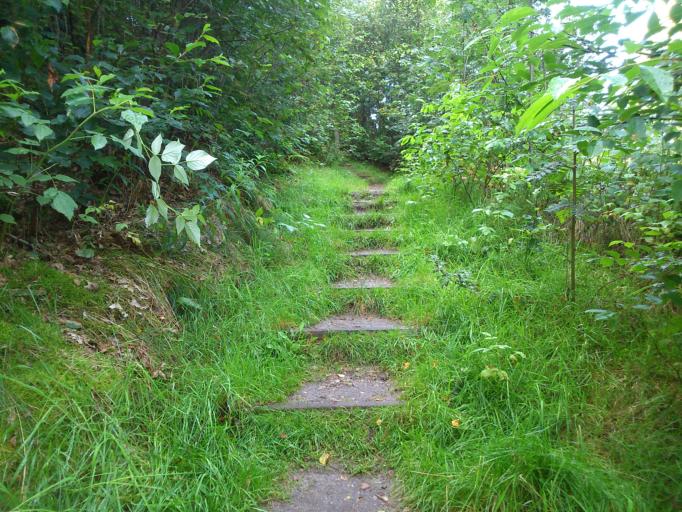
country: DK
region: Central Jutland
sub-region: Ikast-Brande Kommune
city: Brande
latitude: 56.0196
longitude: 9.0924
